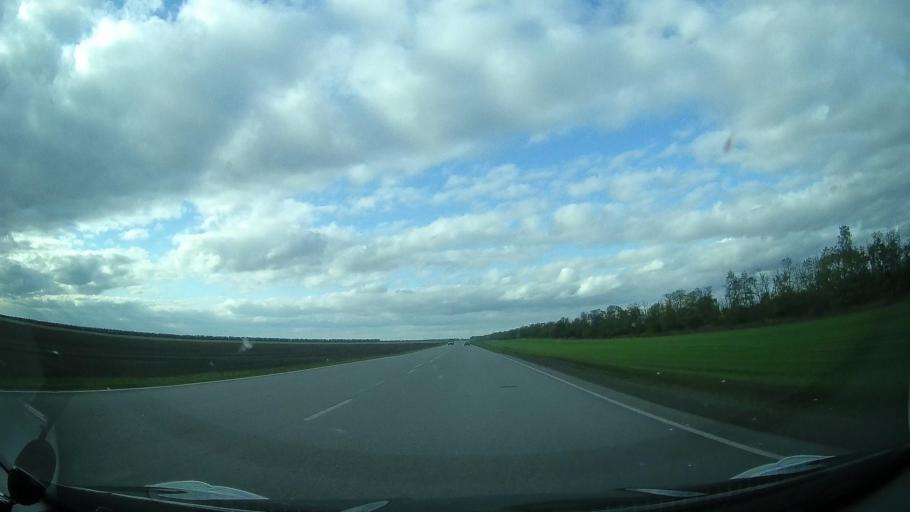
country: RU
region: Rostov
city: Kagal'nitskaya
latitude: 46.8990
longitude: 40.1246
